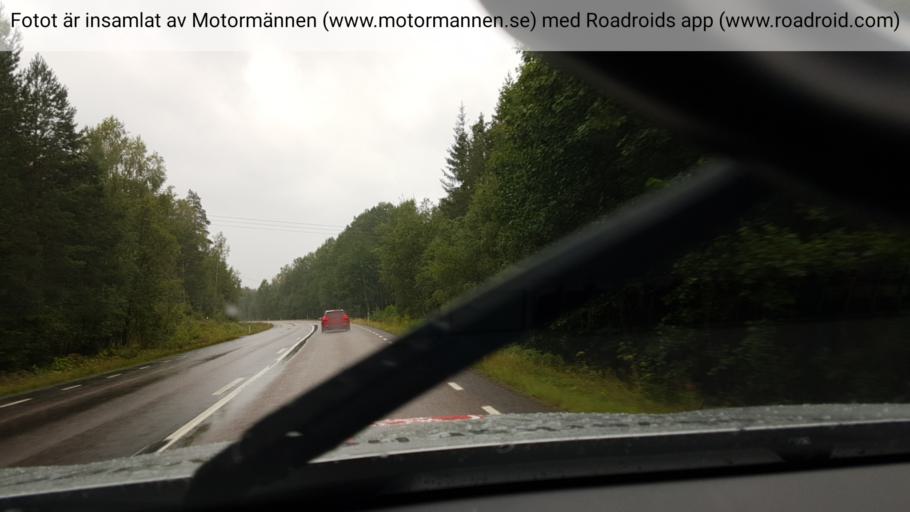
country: SE
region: Vaestra Goetaland
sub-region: Amals Kommun
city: Amal
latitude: 59.0623
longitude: 12.6535
